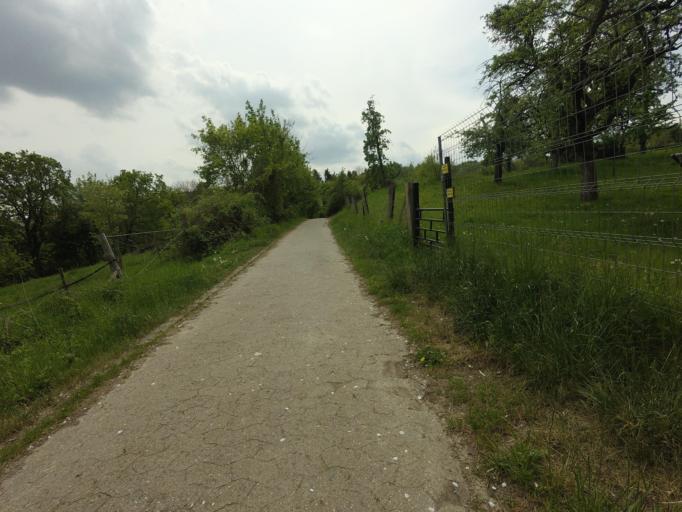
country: DE
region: Lower Saxony
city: Diekholzen
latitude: 52.1250
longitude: 9.9100
